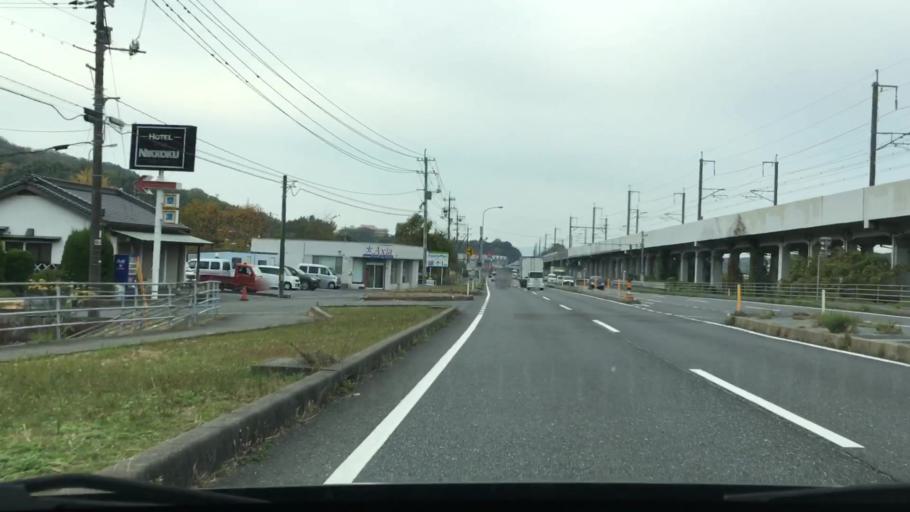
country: JP
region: Yamaguchi
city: Kudamatsu
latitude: 34.0352
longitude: 131.8895
